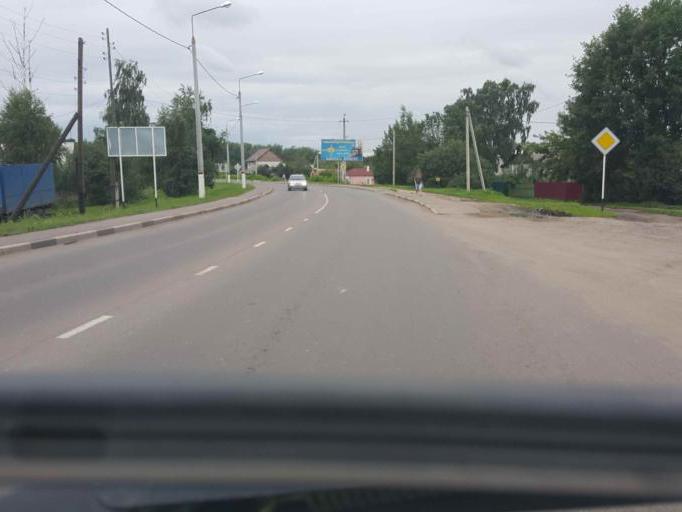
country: RU
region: Tambov
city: Zavoronezhskoye
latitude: 52.8831
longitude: 40.5424
